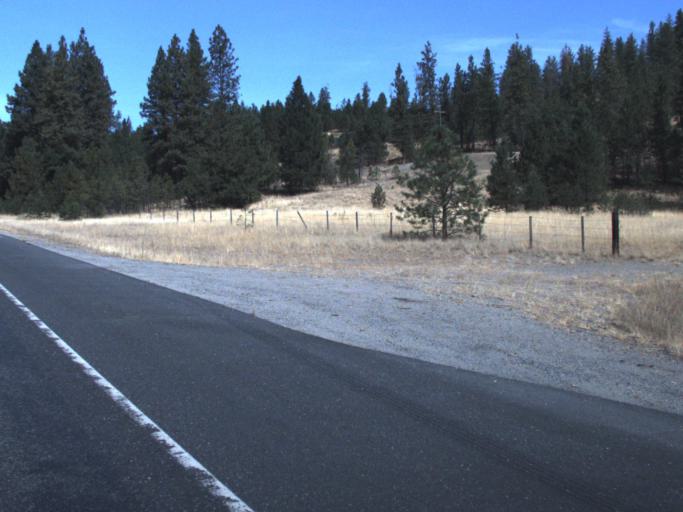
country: US
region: Washington
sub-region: Stevens County
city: Colville
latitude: 48.3949
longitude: -117.8474
